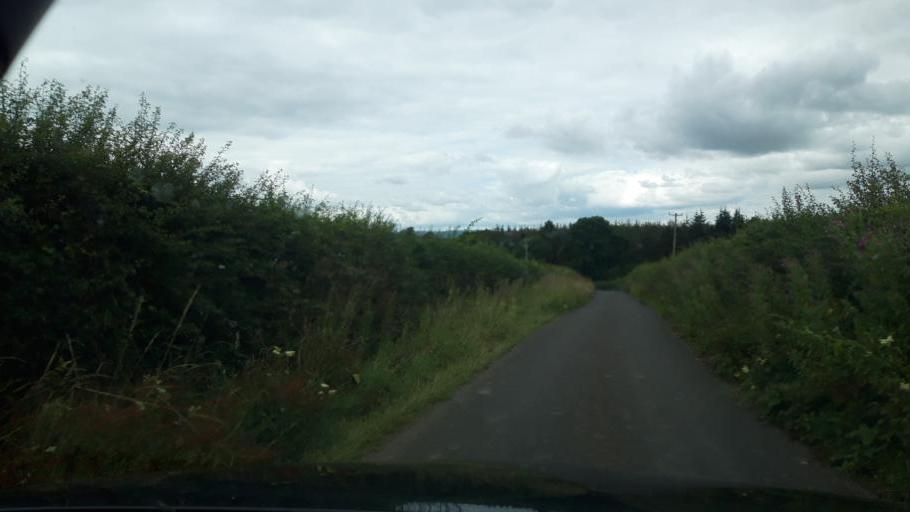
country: IE
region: Leinster
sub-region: Kilkenny
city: Graiguenamanagh
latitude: 52.5929
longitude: -7.0290
